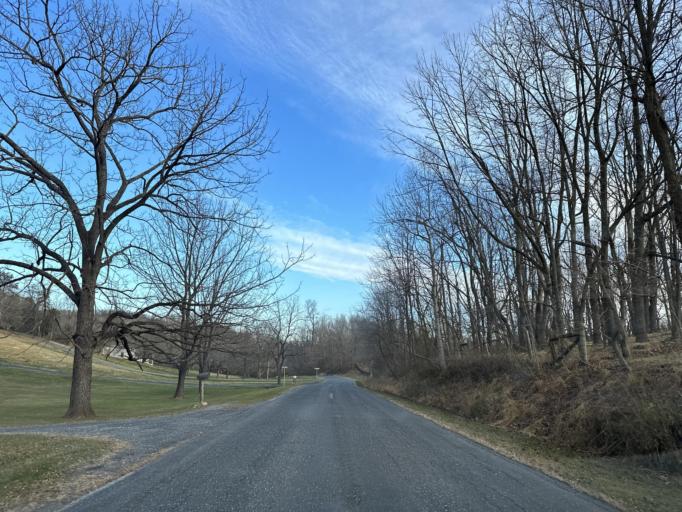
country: US
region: Virginia
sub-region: City of Staunton
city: Staunton
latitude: 38.2198
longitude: -79.2140
